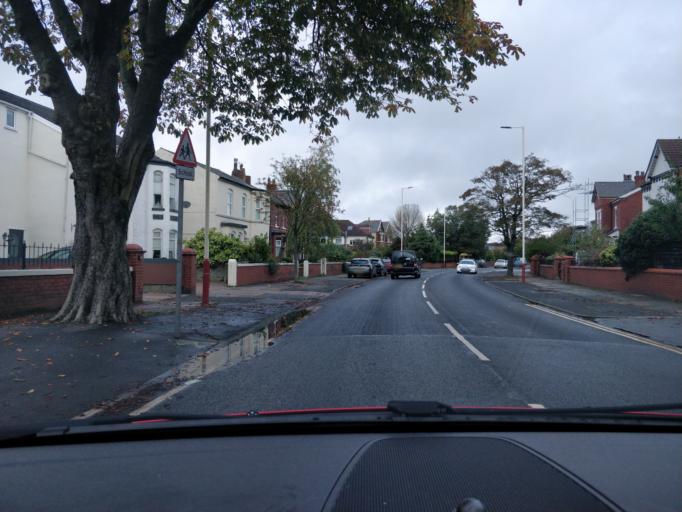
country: GB
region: England
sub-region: Sefton
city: Southport
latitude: 53.6237
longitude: -3.0128
